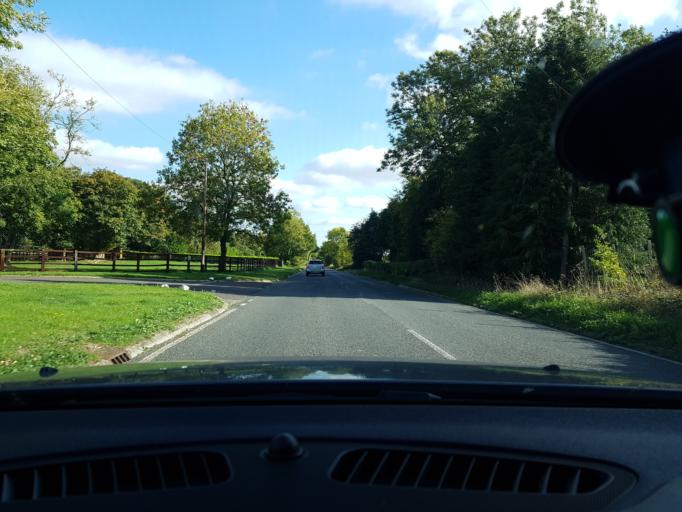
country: GB
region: England
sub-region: Wiltshire
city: Aldbourne
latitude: 51.4929
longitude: -1.5779
